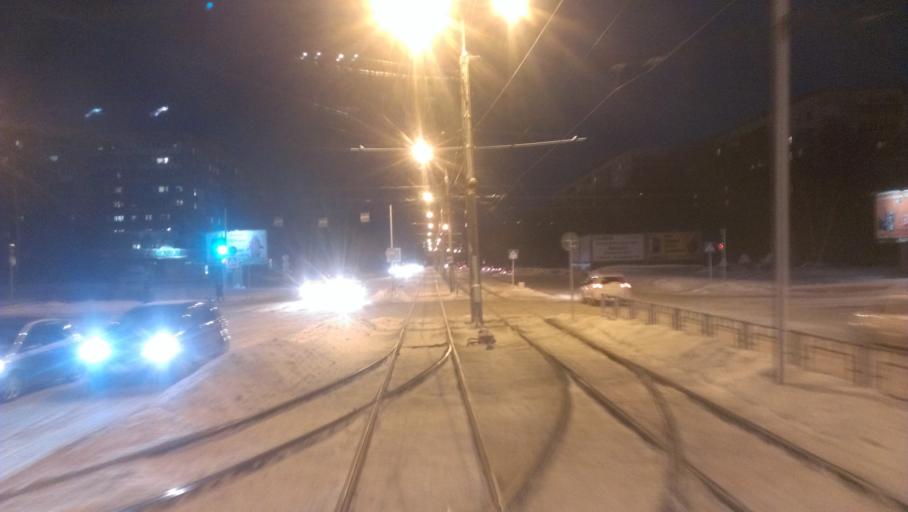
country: RU
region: Altai Krai
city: Novosilikatnyy
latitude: 53.3710
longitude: 83.6776
